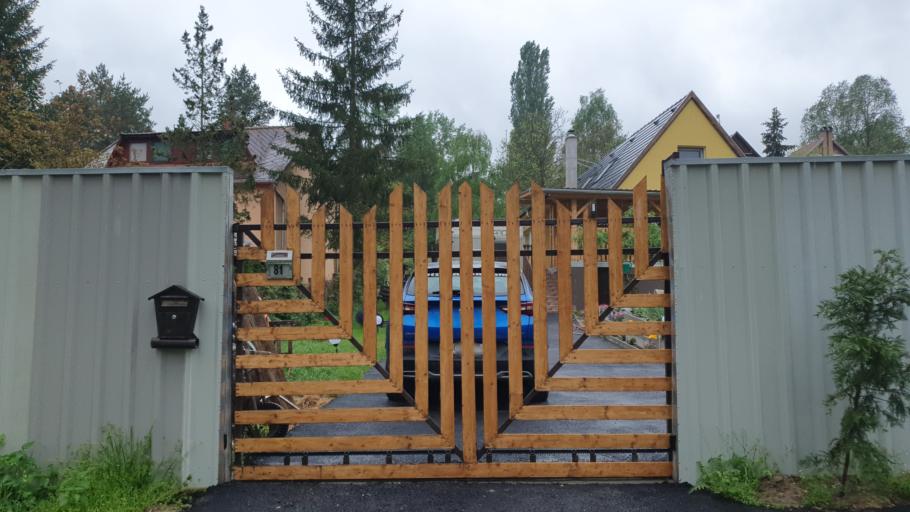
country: HU
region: Komarom-Esztergom
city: Esztergom
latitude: 47.7957
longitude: 18.8064
